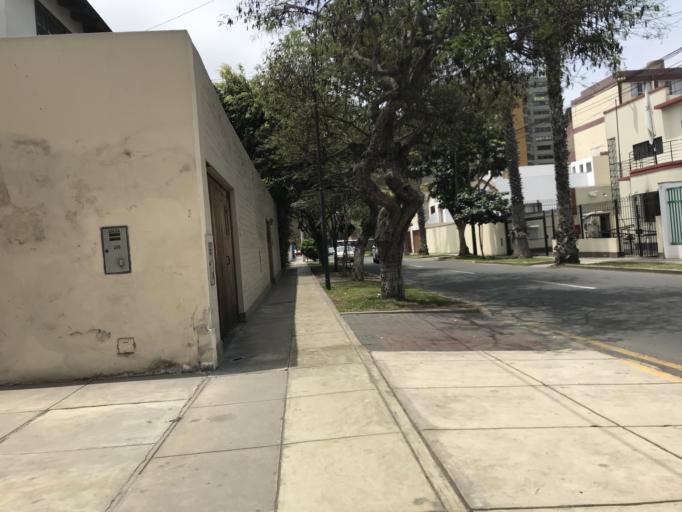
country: PE
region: Lima
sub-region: Lima
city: San Isidro
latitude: -12.0915
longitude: -77.0370
